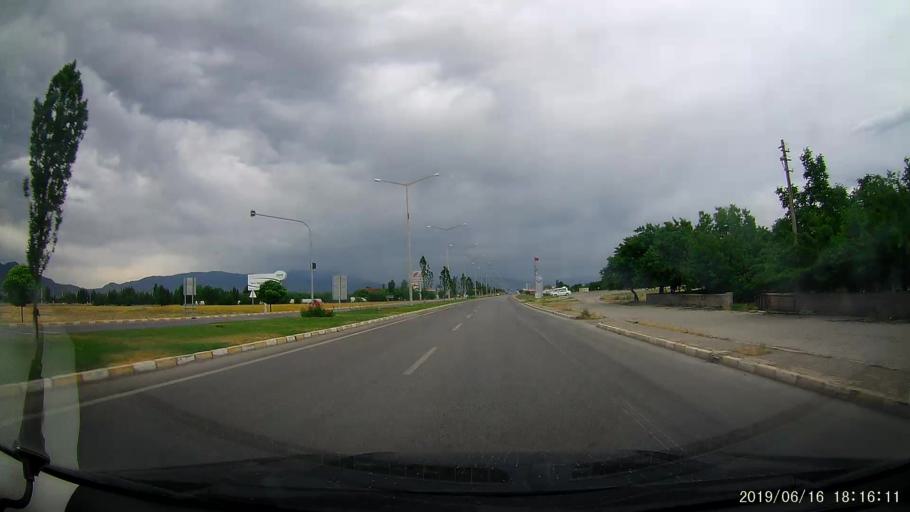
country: TR
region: Erzincan
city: Erzincan
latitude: 39.7270
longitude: 39.5511
